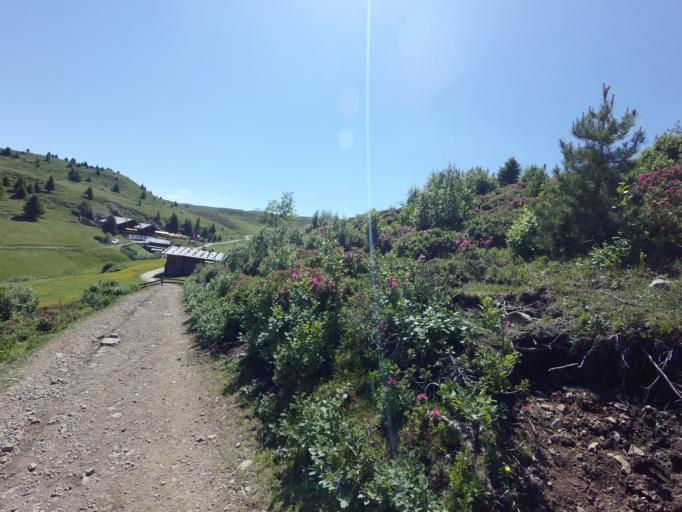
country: IT
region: Trentino-Alto Adige
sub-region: Bolzano
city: Castelrotto
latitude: 46.5593
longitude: 11.6056
